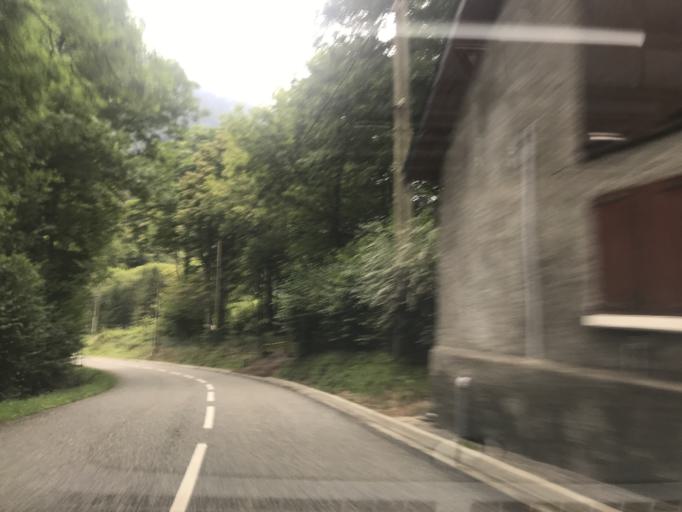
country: FR
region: Midi-Pyrenees
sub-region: Departement de la Haute-Garonne
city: Bagneres-de-Luchon
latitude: 42.7705
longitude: 0.6486
